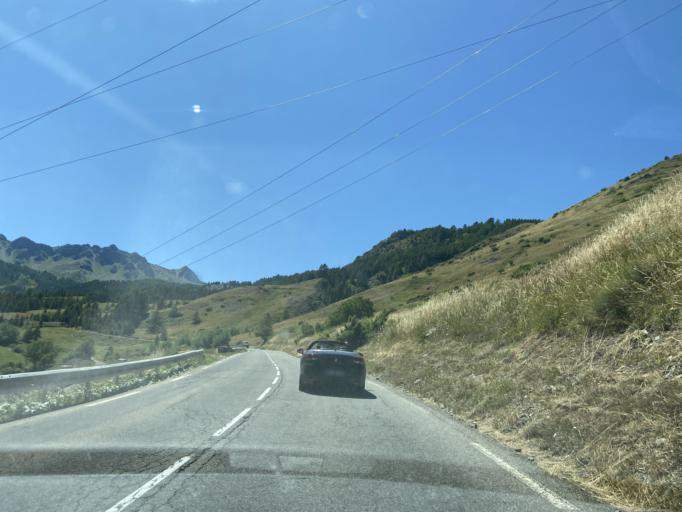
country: FR
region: Provence-Alpes-Cote d'Azur
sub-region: Departement des Hautes-Alpes
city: Guillestre
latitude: 44.5862
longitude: 6.6858
